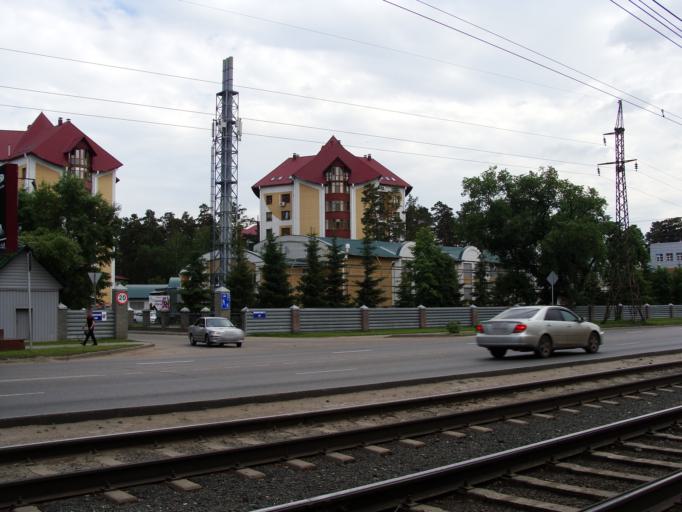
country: RU
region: Altai Krai
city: Zaton
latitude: 53.2876
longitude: 83.7549
